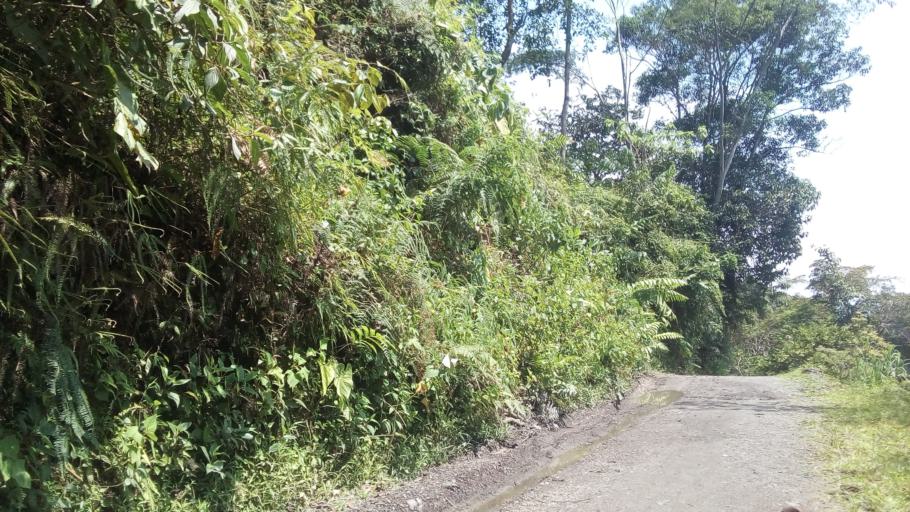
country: CO
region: Boyaca
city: Otanche
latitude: 5.6257
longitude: -74.2366
